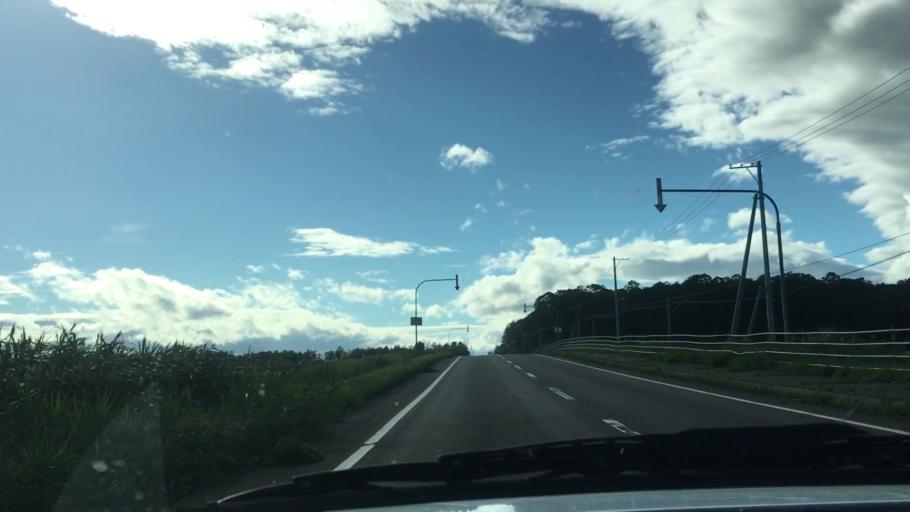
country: JP
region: Hokkaido
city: Otofuke
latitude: 43.1562
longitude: 143.1865
